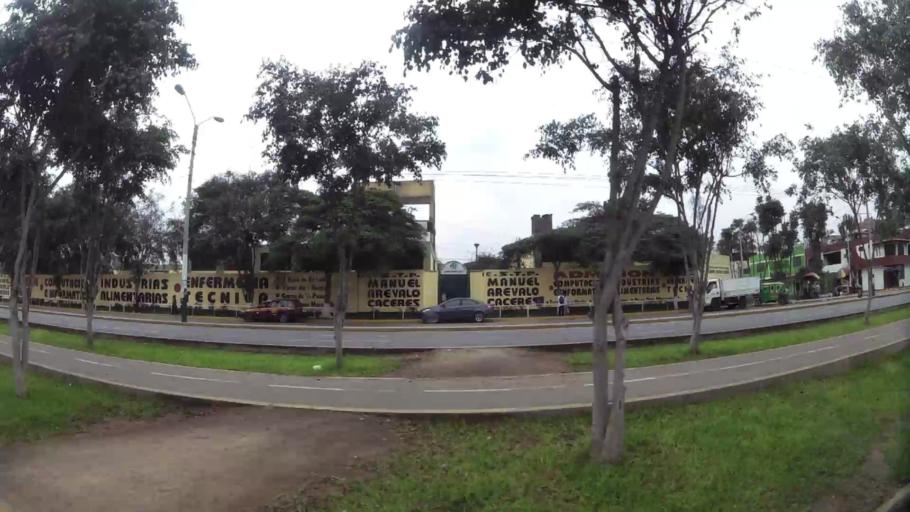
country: PE
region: Lima
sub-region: Lima
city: Independencia
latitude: -11.9837
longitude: -77.0734
